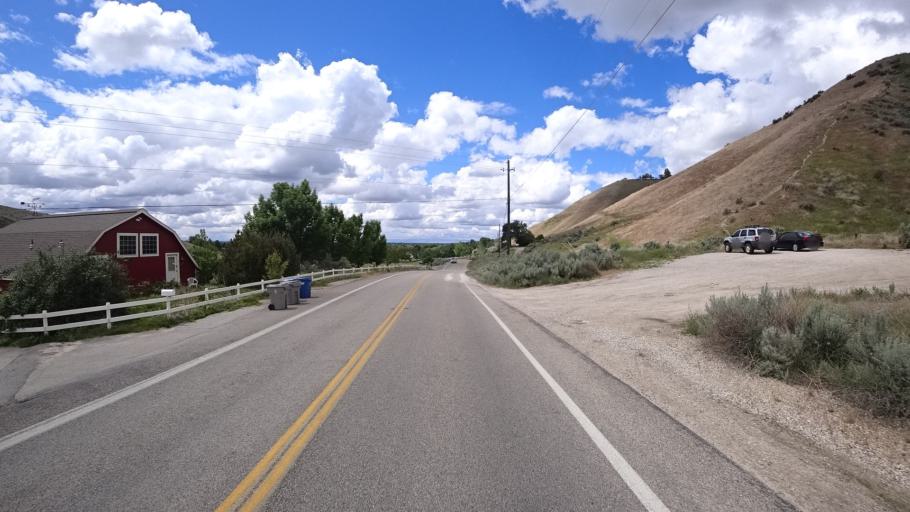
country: US
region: Idaho
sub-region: Ada County
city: Garden City
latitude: 43.6617
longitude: -116.2265
